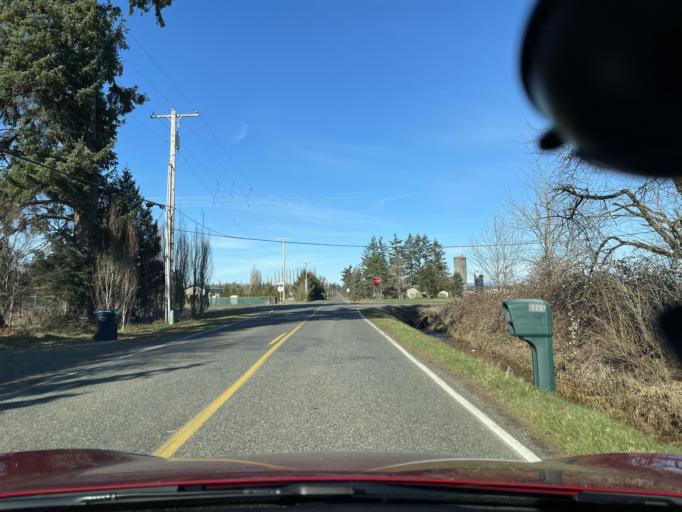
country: US
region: Washington
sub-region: Whatcom County
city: Lynden
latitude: 48.9643
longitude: -122.5302
